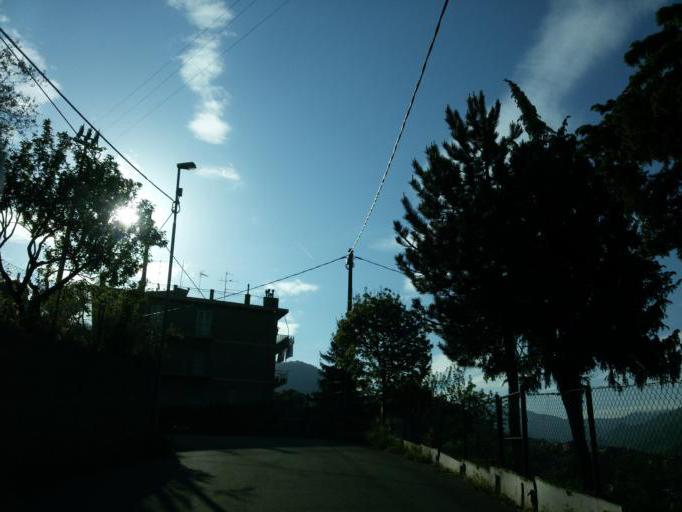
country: IT
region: Liguria
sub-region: Provincia di Genova
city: Piccarello
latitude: 44.4641
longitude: 8.9758
